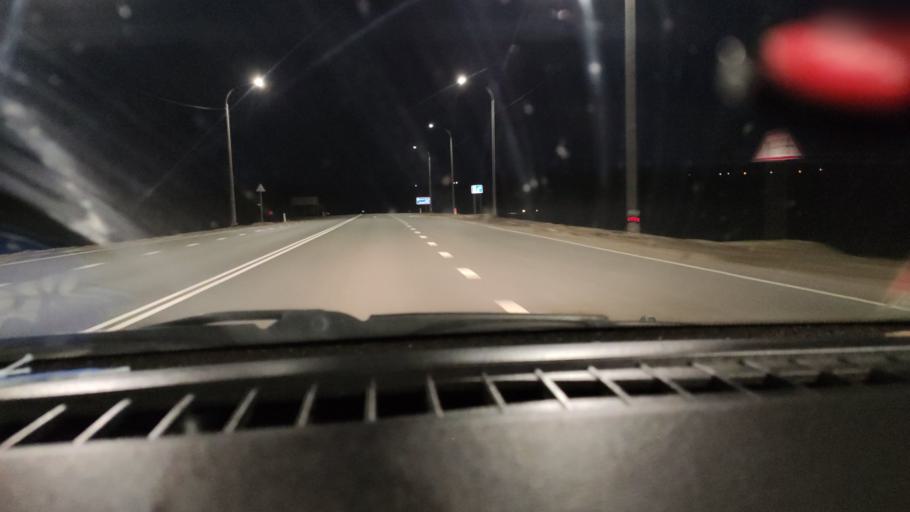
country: RU
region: Saratov
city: Shikhany
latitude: 52.1281
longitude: 47.2361
